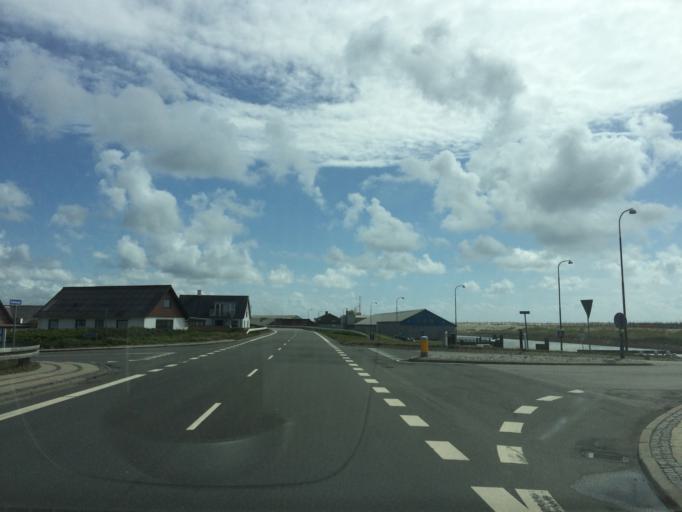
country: DK
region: Central Jutland
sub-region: Holstebro Kommune
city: Ulfborg
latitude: 56.3719
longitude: 8.1209
